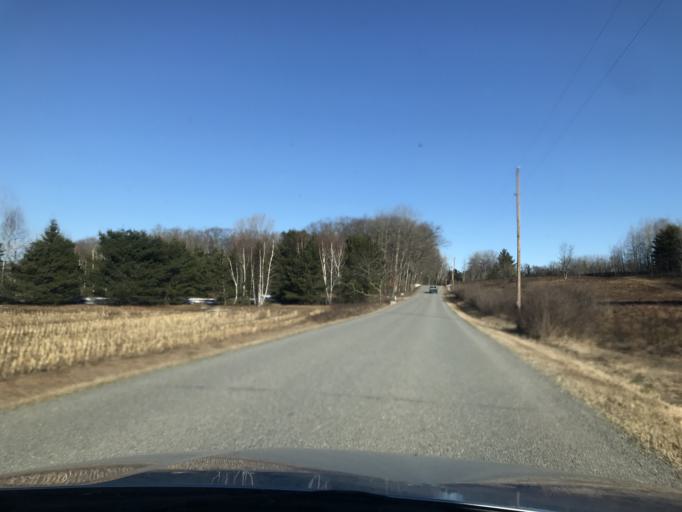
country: US
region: Wisconsin
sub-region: Marinette County
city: Niagara
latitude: 45.3858
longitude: -88.0432
